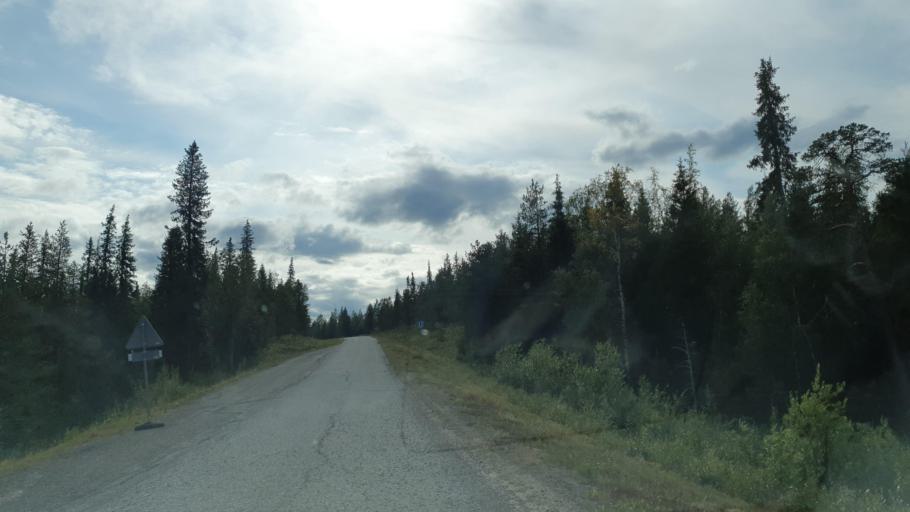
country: FI
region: Lapland
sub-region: Tunturi-Lappi
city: Muonio
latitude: 67.7042
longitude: 24.1222
